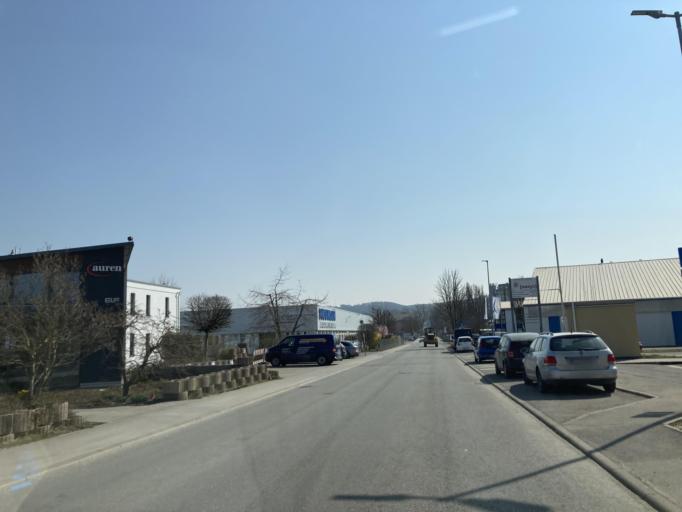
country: DE
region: Baden-Wuerttemberg
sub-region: Tuebingen Region
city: Rottenburg
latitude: 48.4794
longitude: 8.9523
